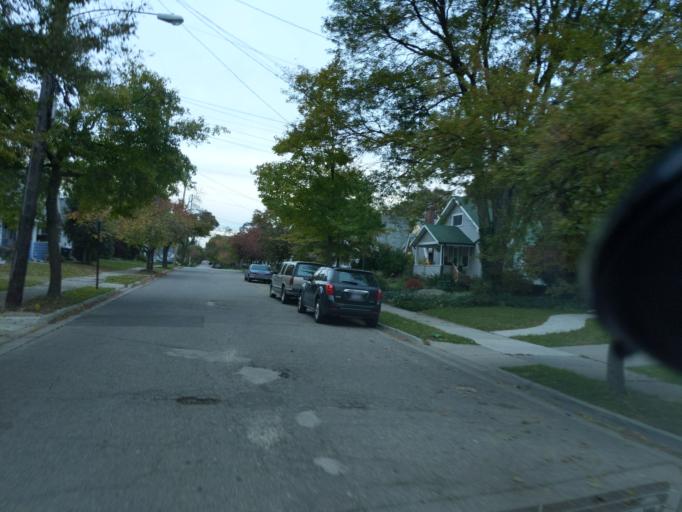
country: US
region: Michigan
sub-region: Ingham County
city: Lansing
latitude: 42.7352
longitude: -84.5200
